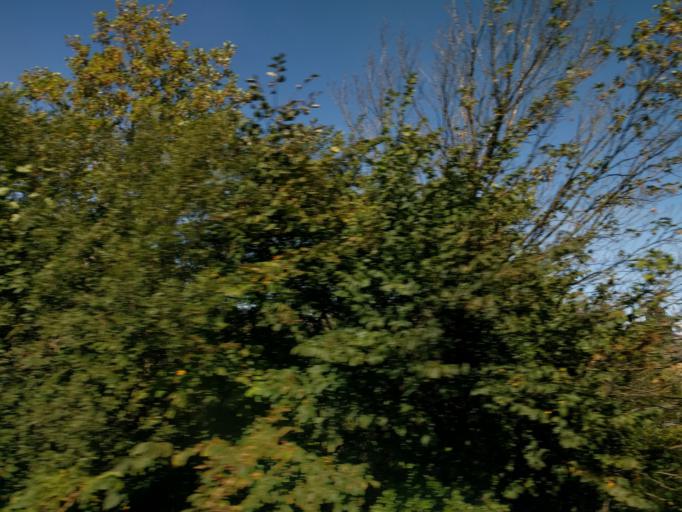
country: DK
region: South Denmark
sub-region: Nyborg Kommune
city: Ullerslev
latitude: 55.3541
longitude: 10.6710
